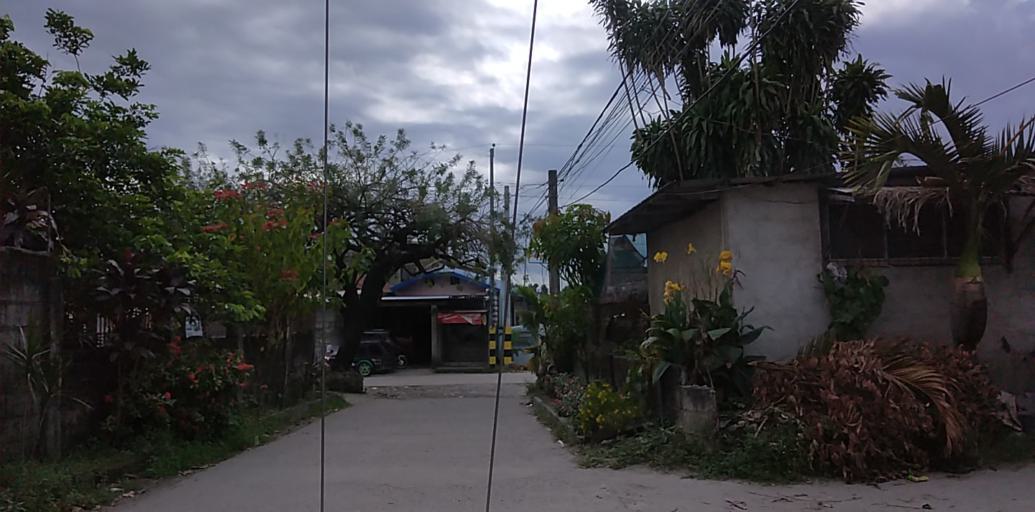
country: PH
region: Central Luzon
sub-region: Province of Pampanga
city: Pulung Santol
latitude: 15.0492
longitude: 120.5557
